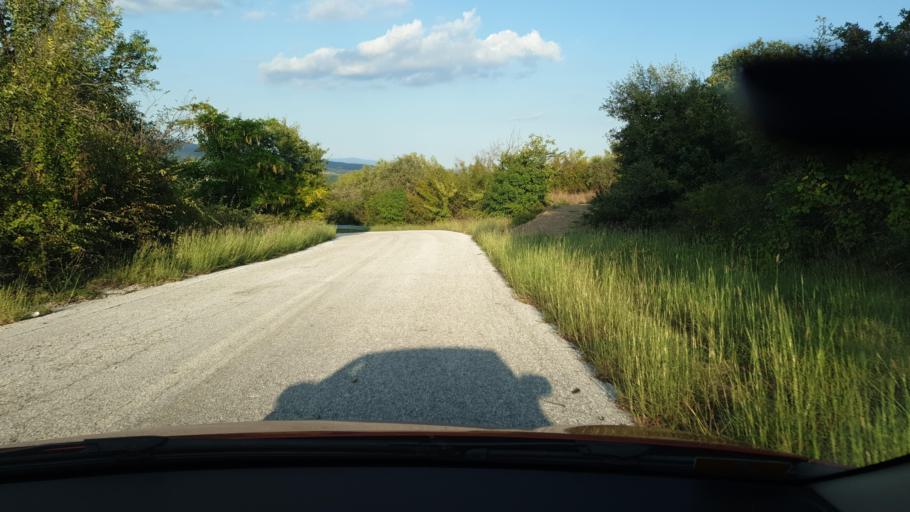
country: GR
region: Central Macedonia
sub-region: Nomos Chalkidikis
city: Galatista
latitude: 40.5593
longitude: 23.2826
